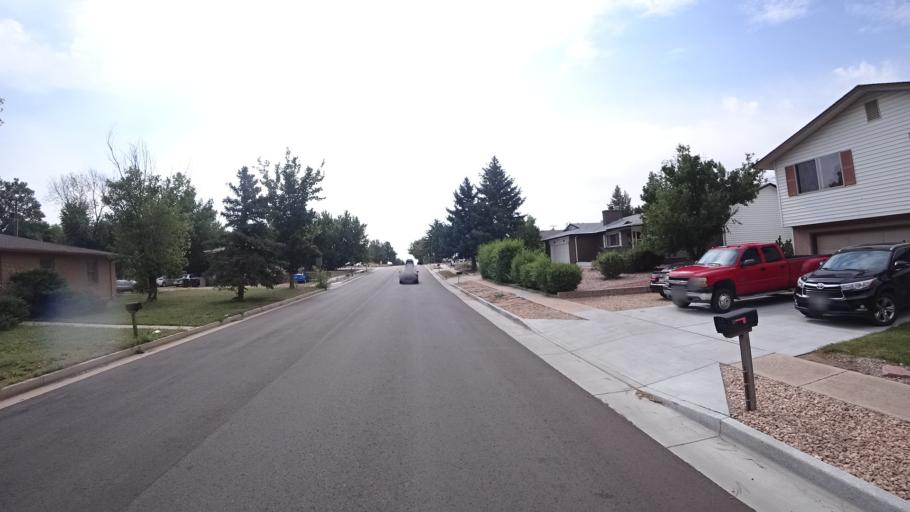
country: US
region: Colorado
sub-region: El Paso County
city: Colorado Springs
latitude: 38.8885
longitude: -104.8012
